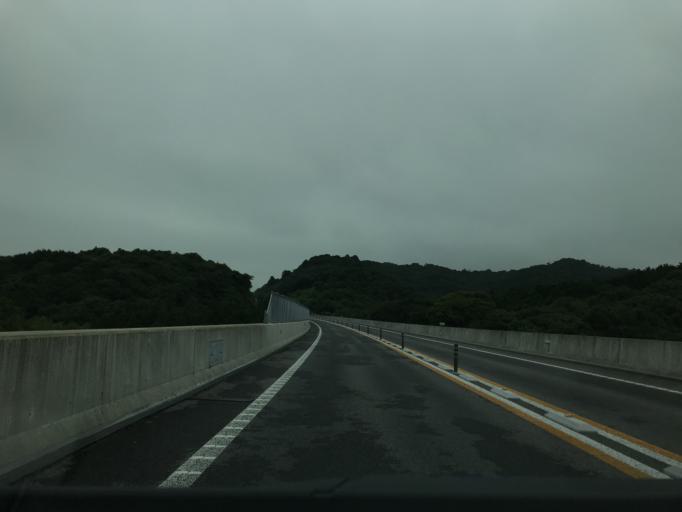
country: JP
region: Fukuoka
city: Nakatsu
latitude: 33.5045
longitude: 131.2991
